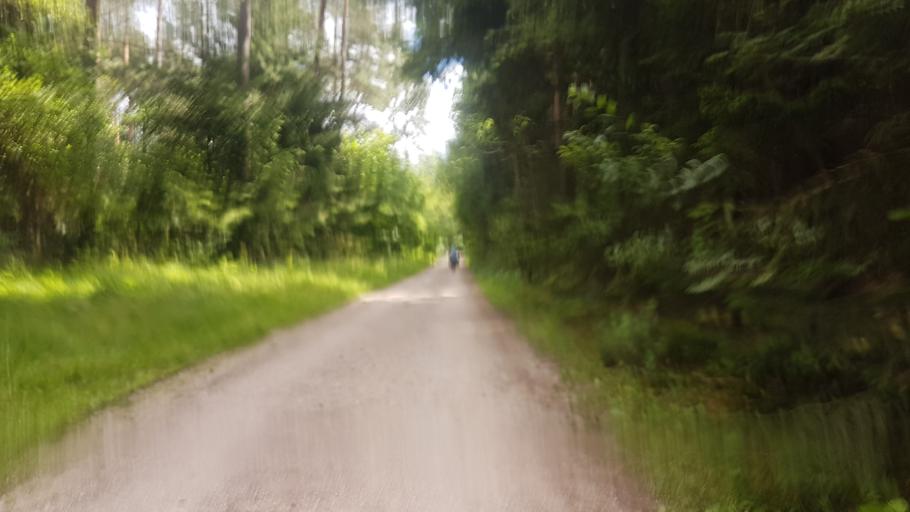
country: DE
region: Bavaria
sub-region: Regierungsbezirk Mittelfranken
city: Pfofeld
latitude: 49.1251
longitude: 10.8270
